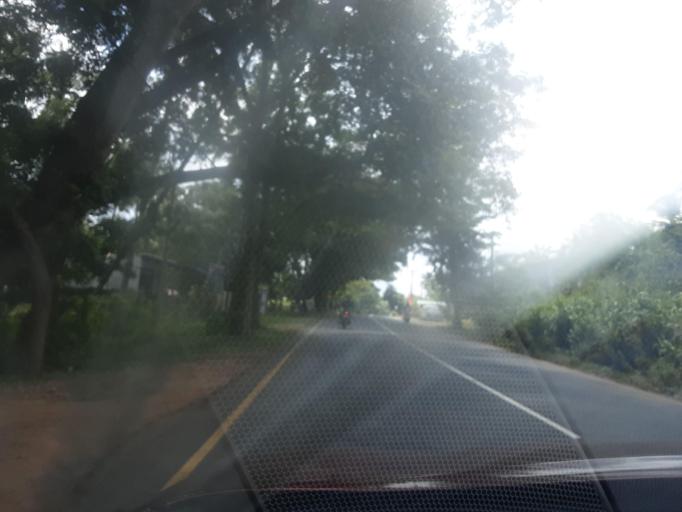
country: LK
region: North Western
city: Kuliyapitiya
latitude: 7.4768
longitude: 80.0066
